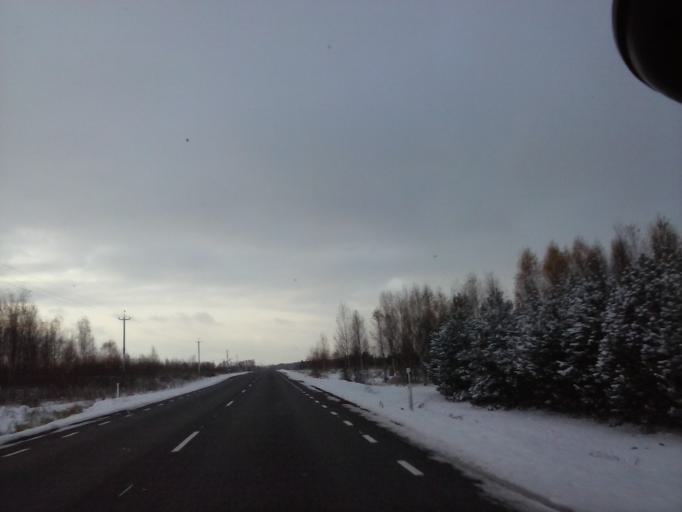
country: EE
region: Tartu
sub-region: UElenurme vald
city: Ulenurme
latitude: 58.3233
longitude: 26.8085
